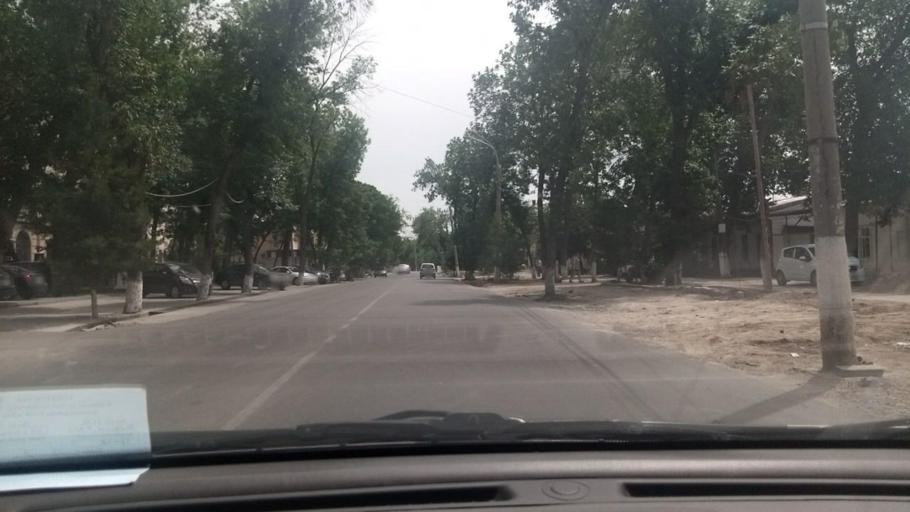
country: UZ
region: Toshkent Shahri
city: Tashkent
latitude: 41.2862
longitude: 69.2833
